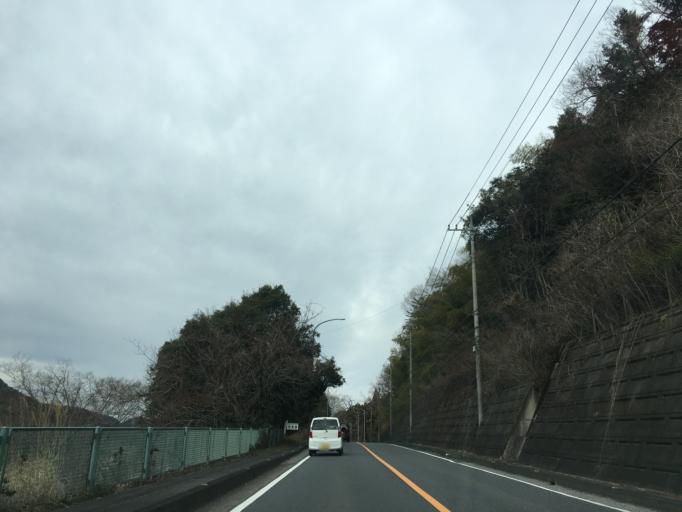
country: JP
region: Saitama
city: Hanno
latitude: 35.8821
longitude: 139.2893
